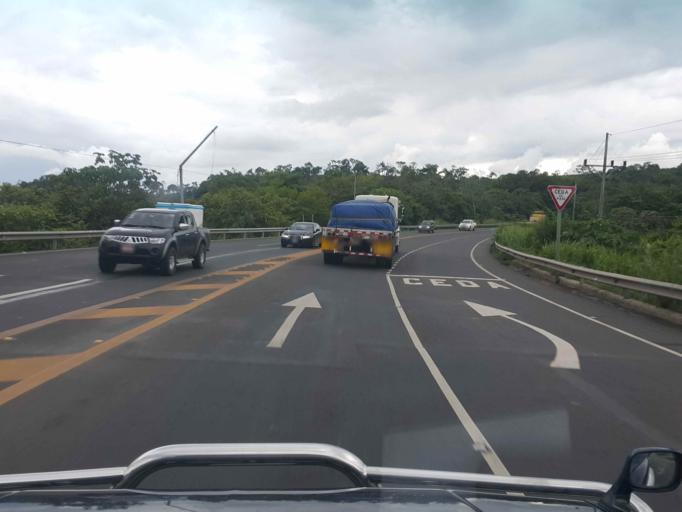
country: CR
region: Puntarenas
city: Esparza
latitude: 9.9135
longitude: -84.6736
